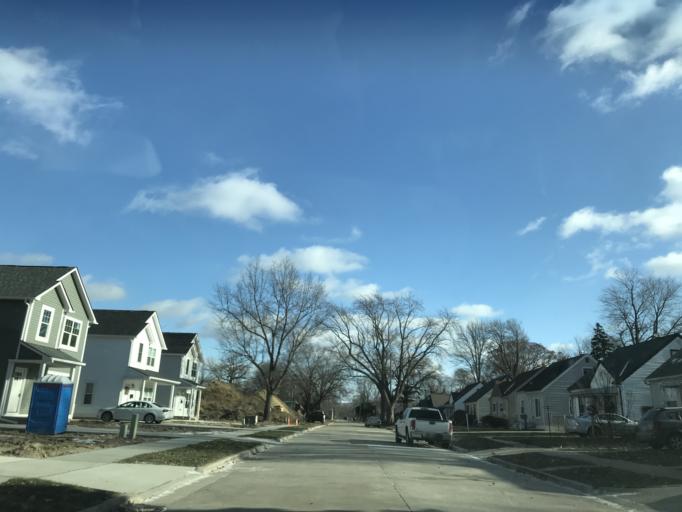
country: US
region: Michigan
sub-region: Oakland County
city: Madison Heights
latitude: 42.4790
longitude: -83.1096
